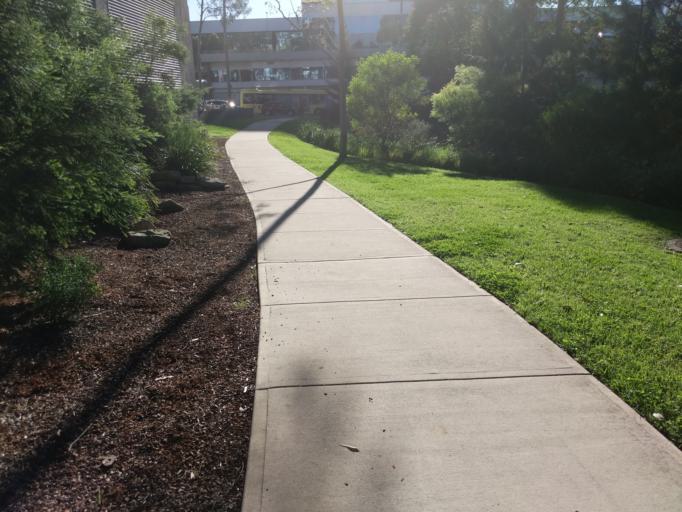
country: AU
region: New South Wales
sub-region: Ryde
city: Macquarie Park
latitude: -33.7743
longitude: 151.1191
